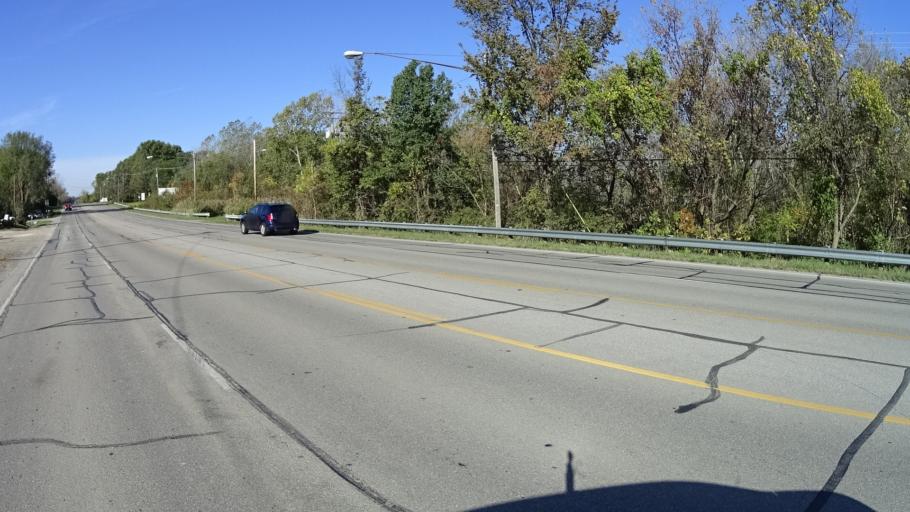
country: US
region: Ohio
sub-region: Lorain County
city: Vermilion-on-the-Lake
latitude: 41.4269
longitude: -82.2886
